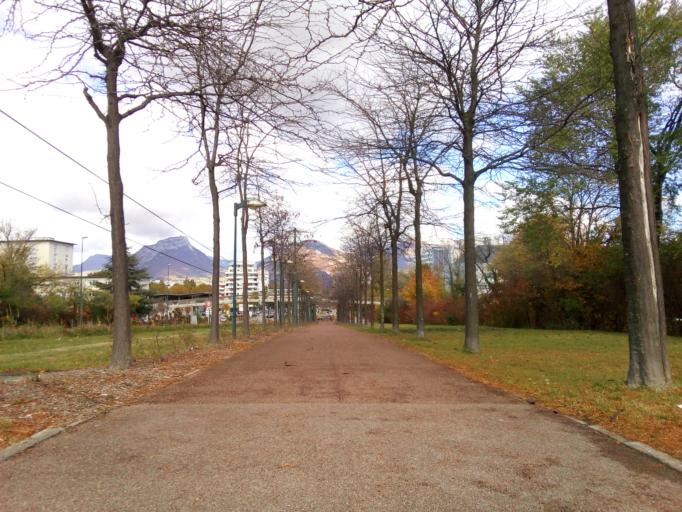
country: FR
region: Rhone-Alpes
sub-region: Departement de l'Isere
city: Grenoble
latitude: 45.1533
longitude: 5.7186
